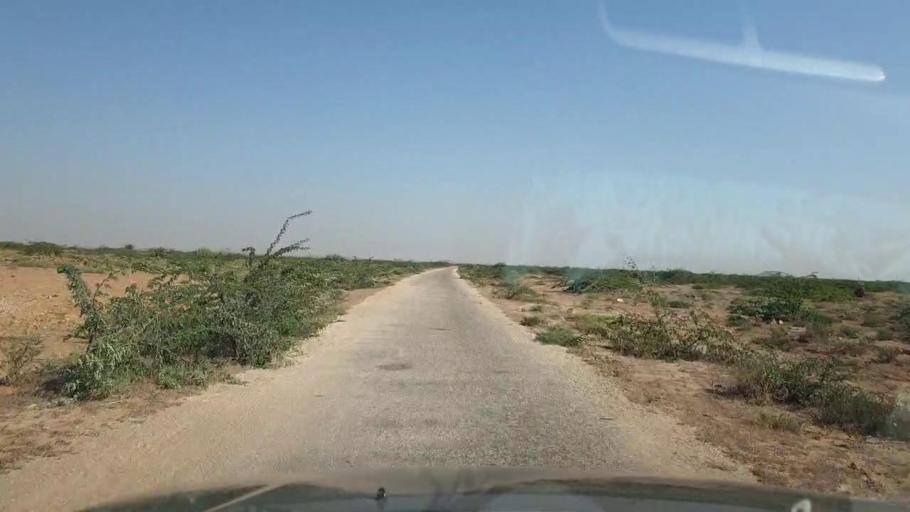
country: PK
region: Sindh
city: Thatta
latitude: 24.8740
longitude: 67.7910
